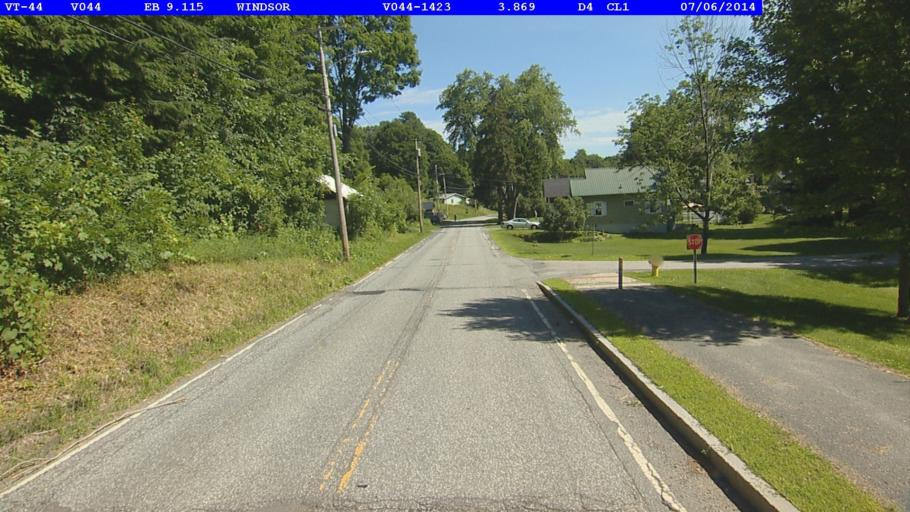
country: US
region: Vermont
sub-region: Windsor County
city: Windsor
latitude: 43.4719
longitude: -72.4043
